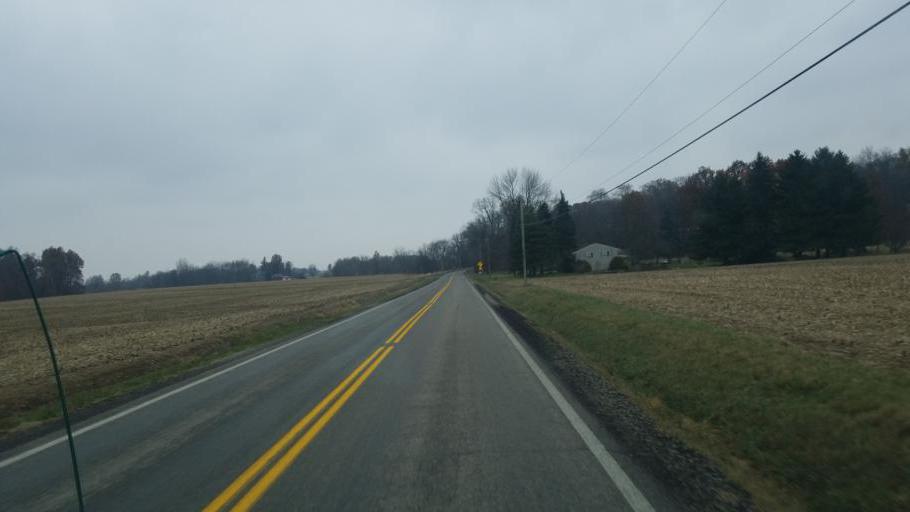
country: US
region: Ohio
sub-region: Crawford County
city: Crestline
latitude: 40.8195
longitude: -82.7911
